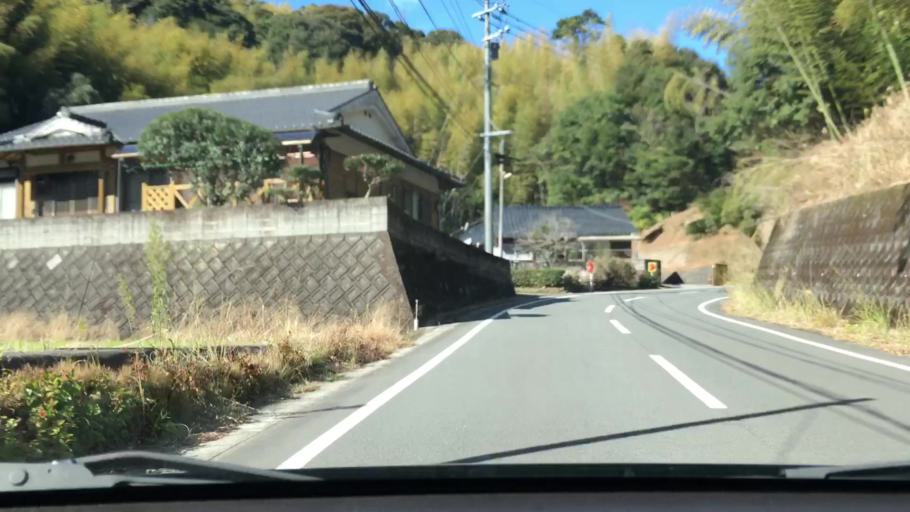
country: JP
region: Kagoshima
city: Ijuin
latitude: 31.7107
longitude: 130.4386
